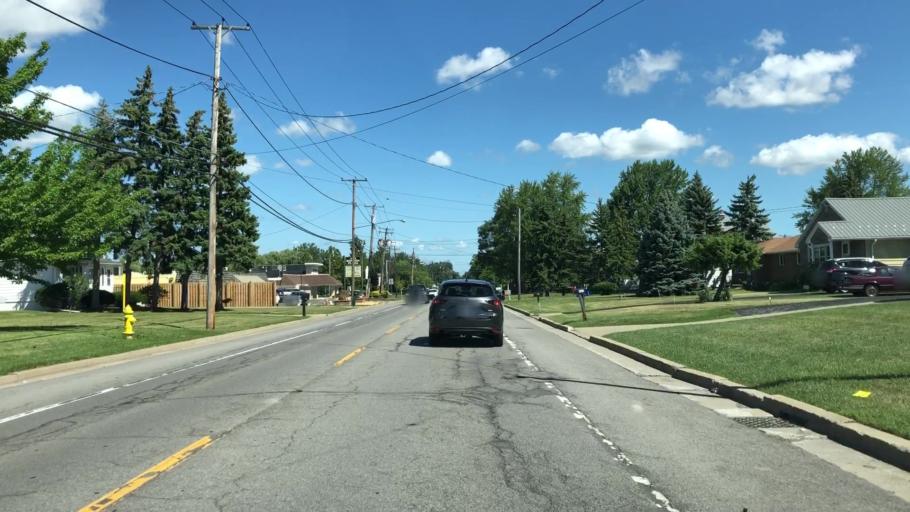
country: US
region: New York
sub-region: Erie County
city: Depew
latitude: 42.8660
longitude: -78.7089
